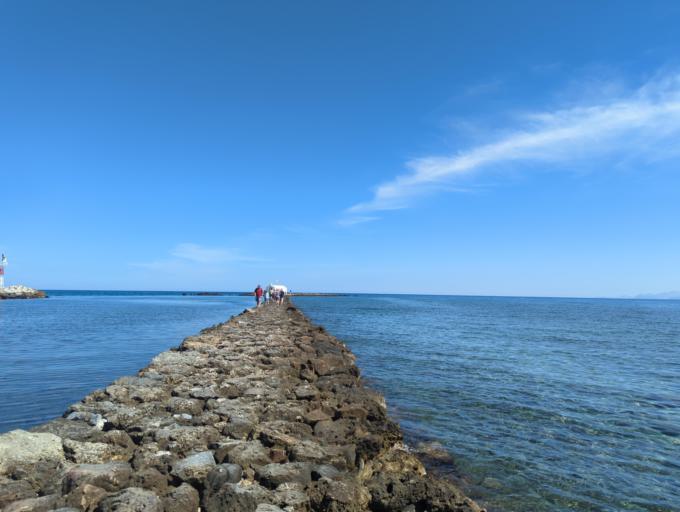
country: GR
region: Crete
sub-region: Nomos Chanias
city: Georgioupolis
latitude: 35.3646
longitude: 24.2623
